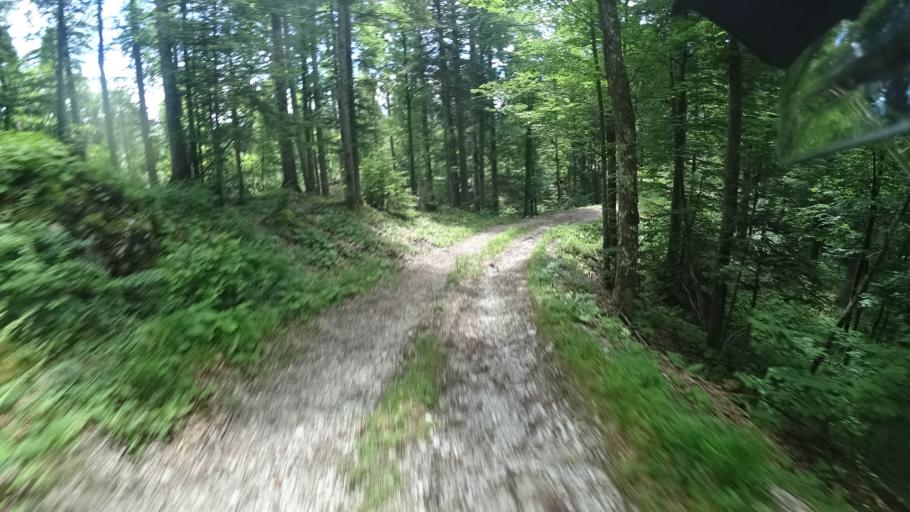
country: SI
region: Osilnica
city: Osilnica
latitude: 45.5149
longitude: 14.6165
